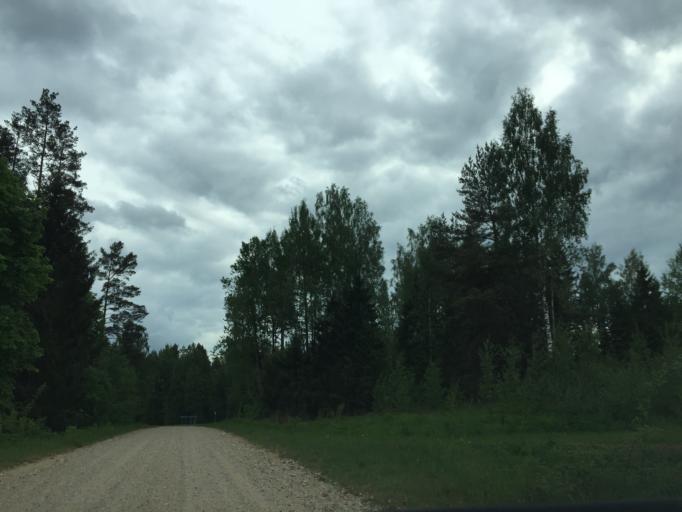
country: LV
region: Dagda
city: Dagda
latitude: 56.1837
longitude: 27.2892
